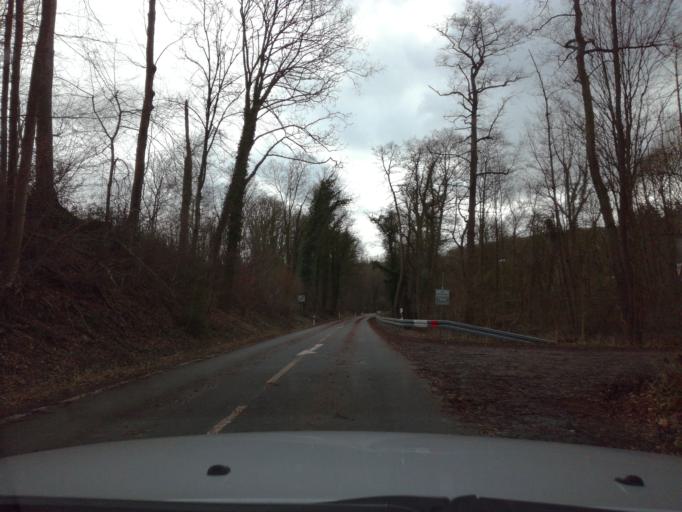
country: DE
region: North Rhine-Westphalia
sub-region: Regierungsbezirk Dusseldorf
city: Velbert
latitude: 51.3685
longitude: 7.0441
